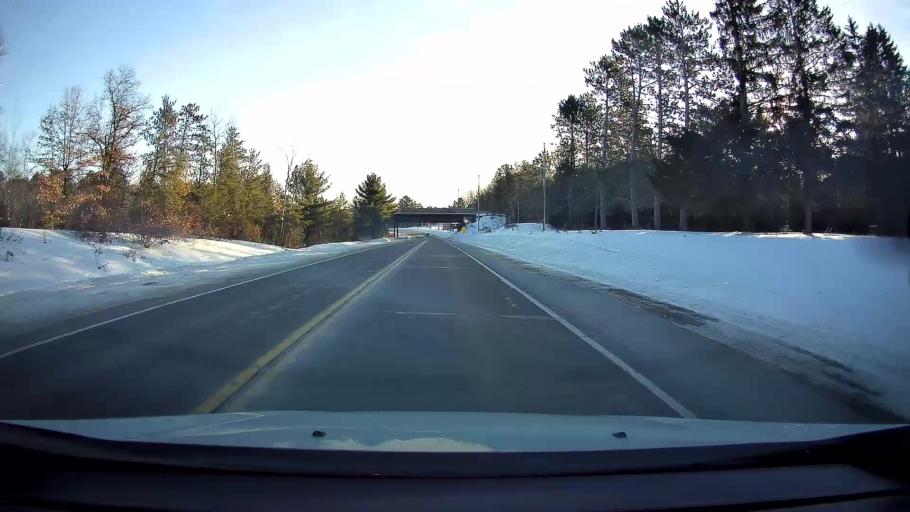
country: US
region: Wisconsin
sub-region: Washburn County
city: Spooner
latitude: 45.9054
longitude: -91.8200
